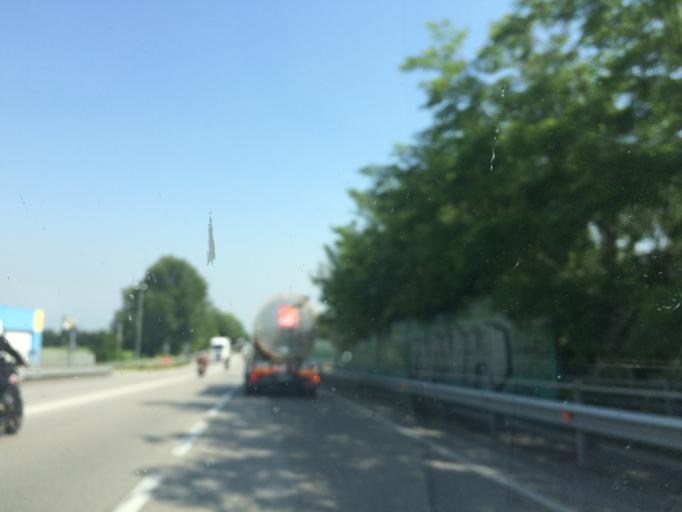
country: IT
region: Veneto
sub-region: Provincia di Padova
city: Cittadella
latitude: 45.6383
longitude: 11.7750
